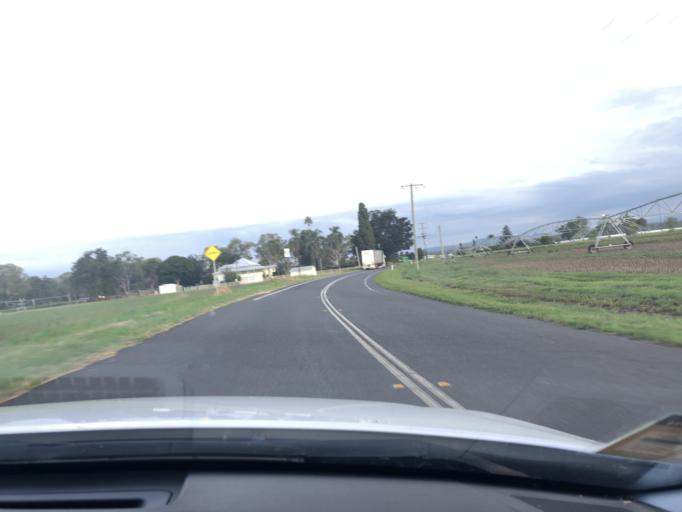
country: AU
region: Queensland
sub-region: Lockyer Valley
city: Gatton
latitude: -27.5784
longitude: 152.3617
